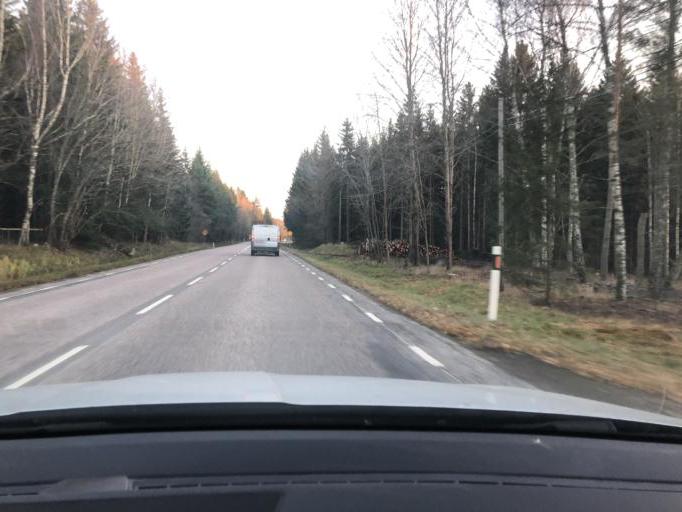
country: SE
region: Soedermanland
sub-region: Strangnas Kommun
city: Akers Styckebruk
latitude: 59.2953
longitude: 17.1036
